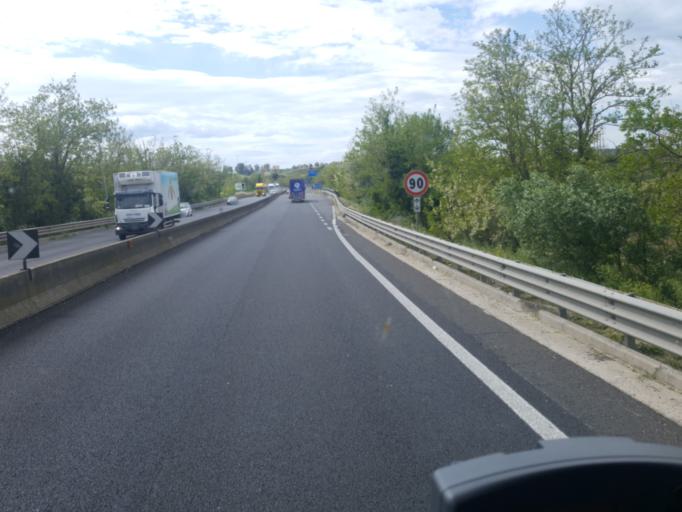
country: IT
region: Latium
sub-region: Citta metropolitana di Roma Capitale
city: La Massimina-Casal Lumbroso
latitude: 41.8833
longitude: 12.3392
